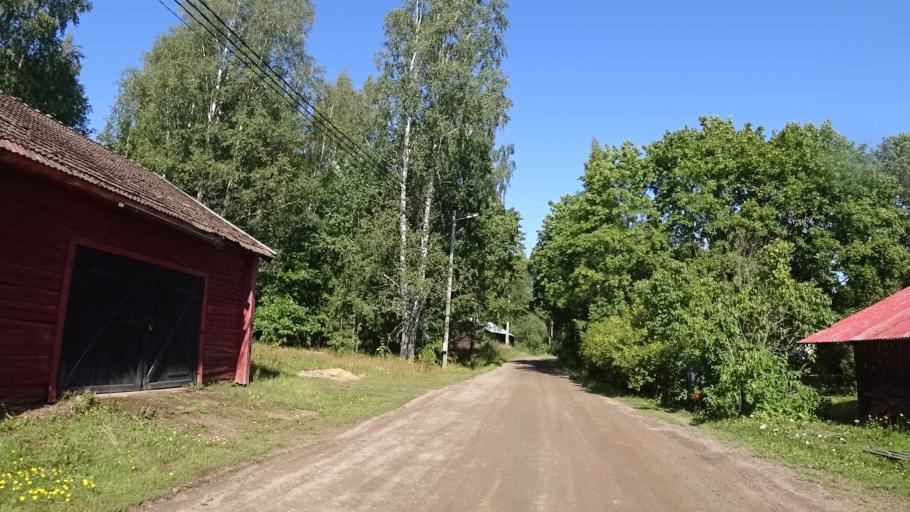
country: FI
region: Kymenlaakso
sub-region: Kotka-Hamina
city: Hamina
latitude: 60.5408
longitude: 27.2197
